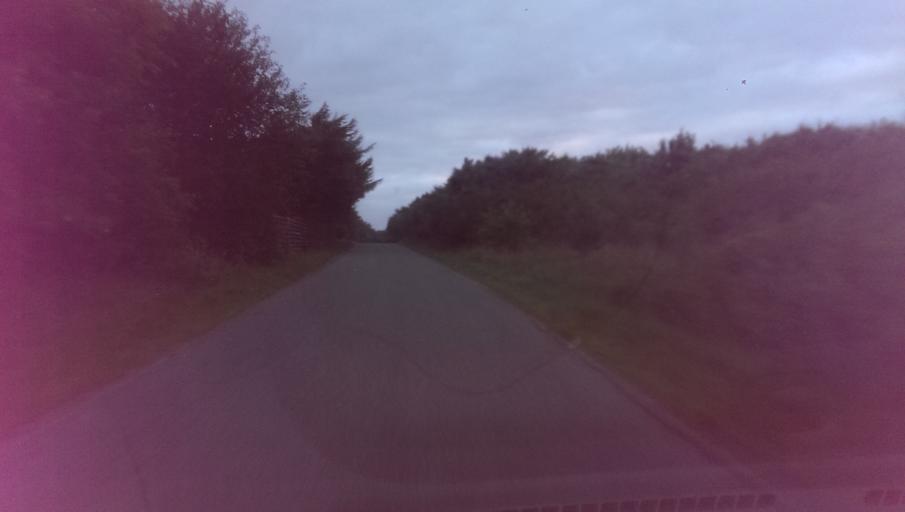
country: DK
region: South Denmark
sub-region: Esbjerg Kommune
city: Tjaereborg
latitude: 55.4856
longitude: 8.5336
